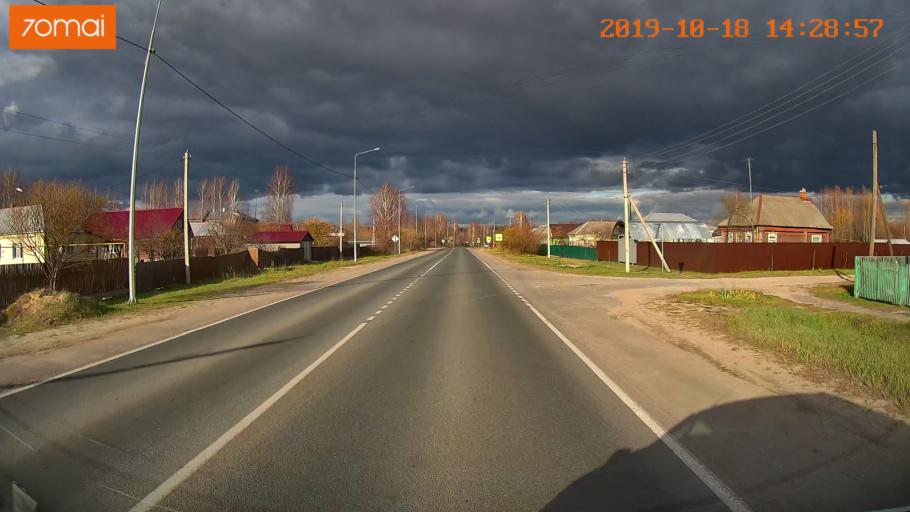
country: RU
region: Rjazan
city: Tuma
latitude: 55.1529
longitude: 40.5551
